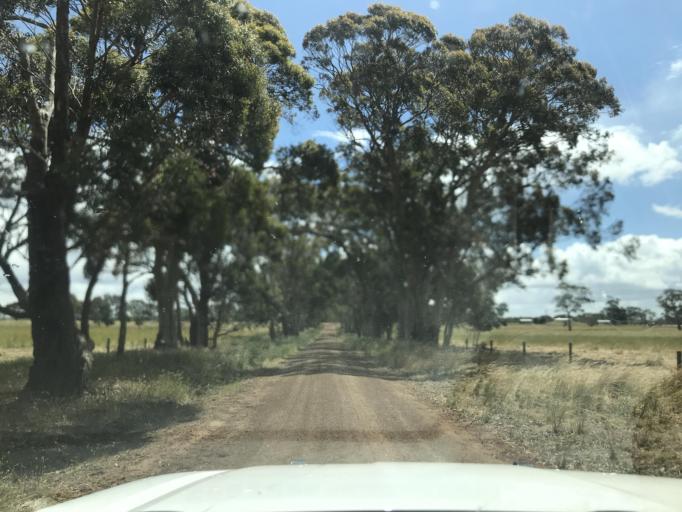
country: AU
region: South Australia
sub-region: Wattle Range
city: Penola
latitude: -37.1243
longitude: 141.2896
